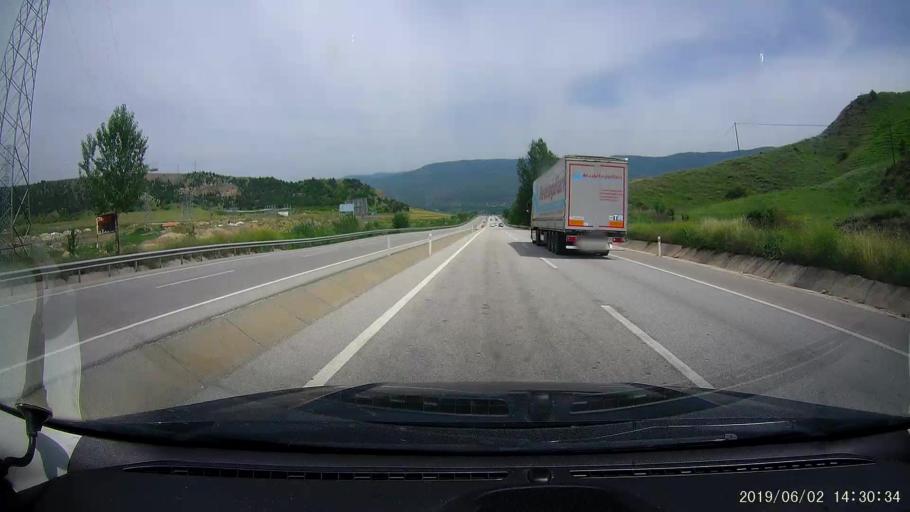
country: TR
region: Kastamonu
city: Tosya
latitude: 41.0169
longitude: 34.1182
